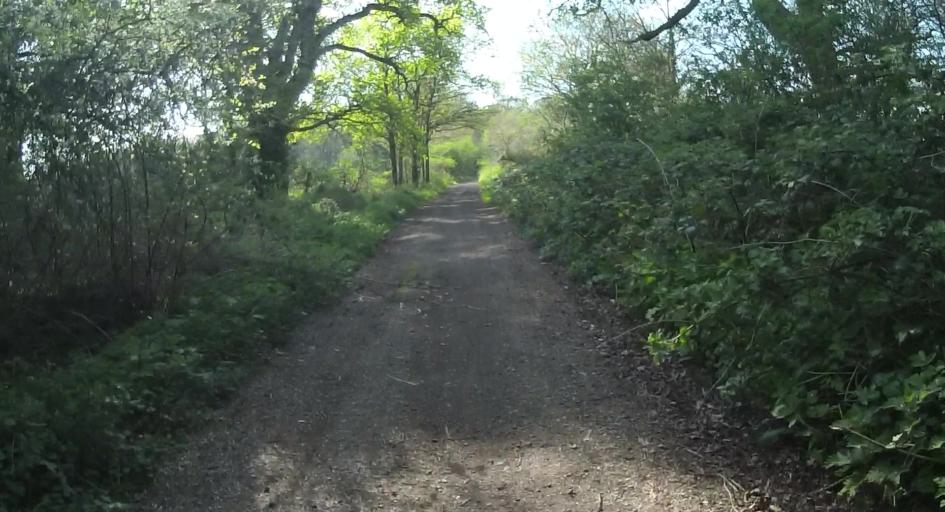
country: GB
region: England
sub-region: West Berkshire
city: Stratfield Mortimer
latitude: 51.3583
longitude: -1.0410
